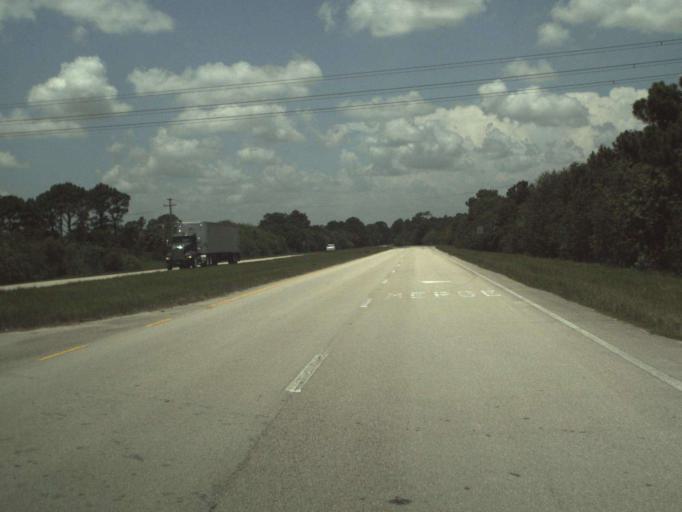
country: US
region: Florida
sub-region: Saint Lucie County
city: Fort Pierce South
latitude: 27.3746
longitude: -80.4162
